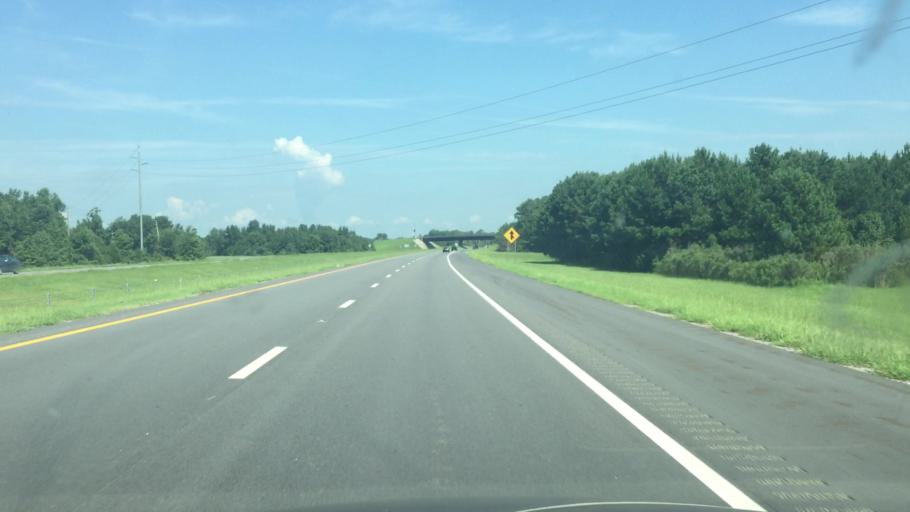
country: US
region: North Carolina
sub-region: Robeson County
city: Maxton
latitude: 34.7114
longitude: -79.3066
